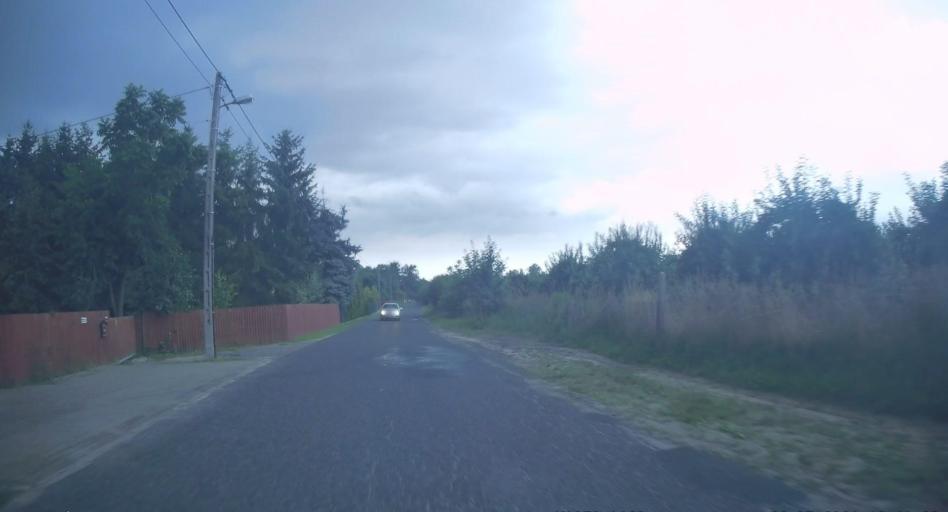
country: PL
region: Lodz Voivodeship
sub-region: Powiat brzezinski
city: Rogow
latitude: 51.8222
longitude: 19.8947
